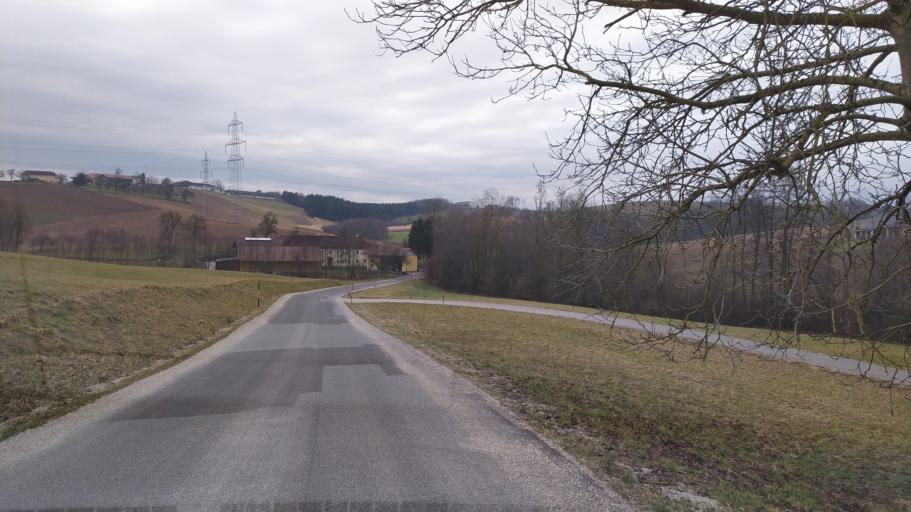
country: AT
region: Lower Austria
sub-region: Politischer Bezirk Amstetten
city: Zeillern
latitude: 48.1336
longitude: 14.7234
